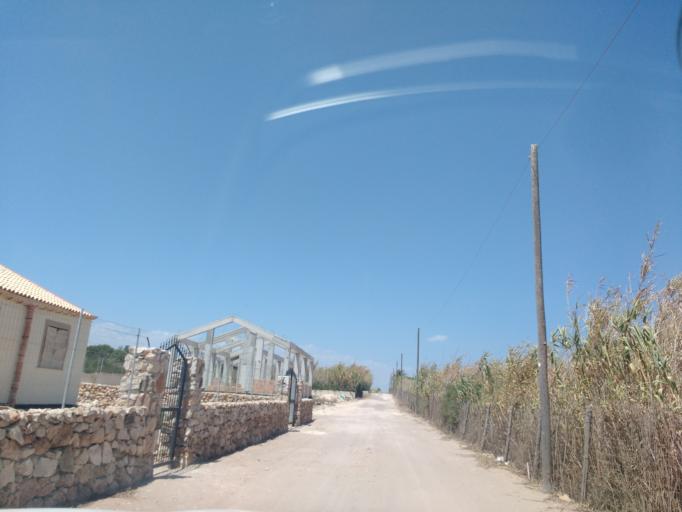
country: IT
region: Sicily
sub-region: Provincia di Siracusa
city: Portopalo di Capo Passero
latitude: 36.6519
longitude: 15.0817
